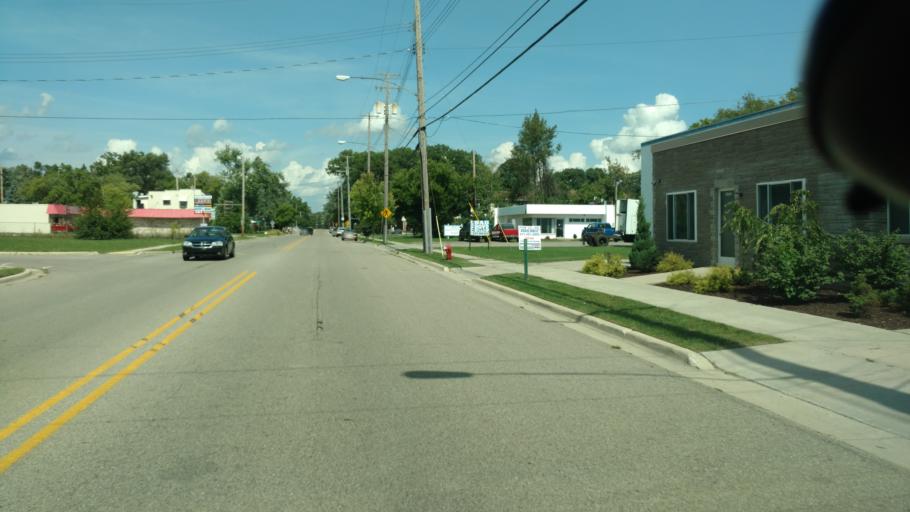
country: US
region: Michigan
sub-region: Ingham County
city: Lansing
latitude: 42.7643
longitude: -84.5557
